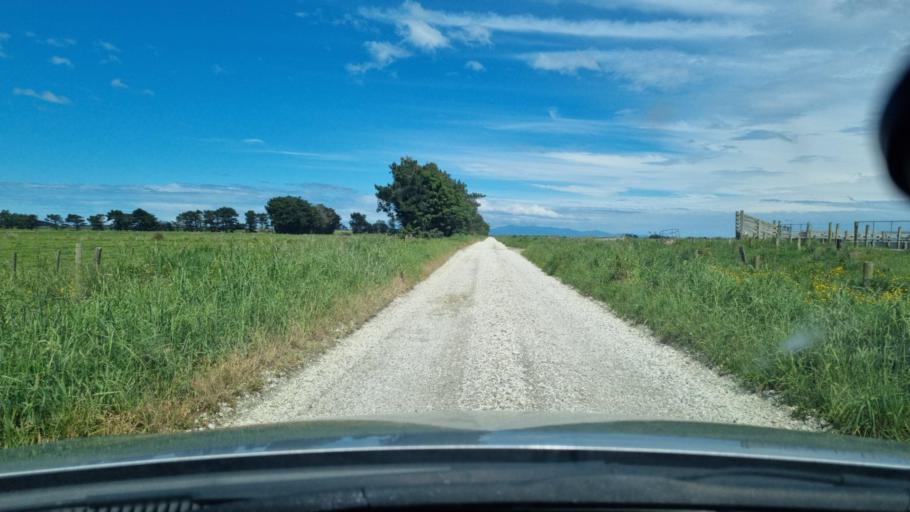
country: NZ
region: Southland
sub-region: Invercargill City
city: Invercargill
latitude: -46.3808
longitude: 168.2693
